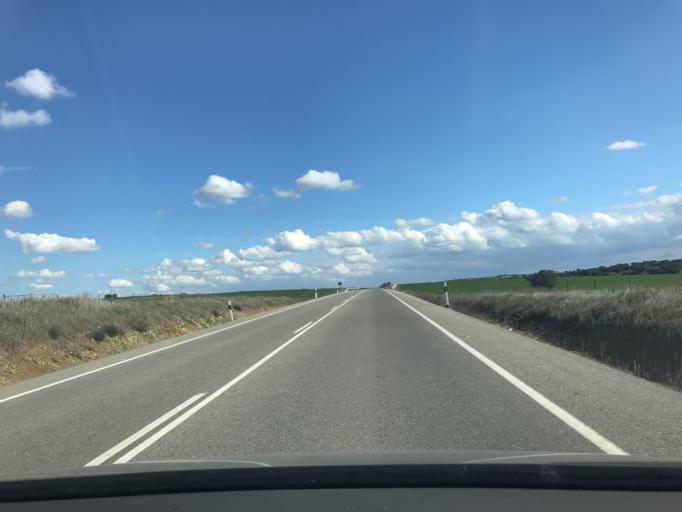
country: ES
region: Extremadura
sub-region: Provincia de Badajoz
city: Granja de Torrehermosa
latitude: 38.2909
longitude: -5.5339
